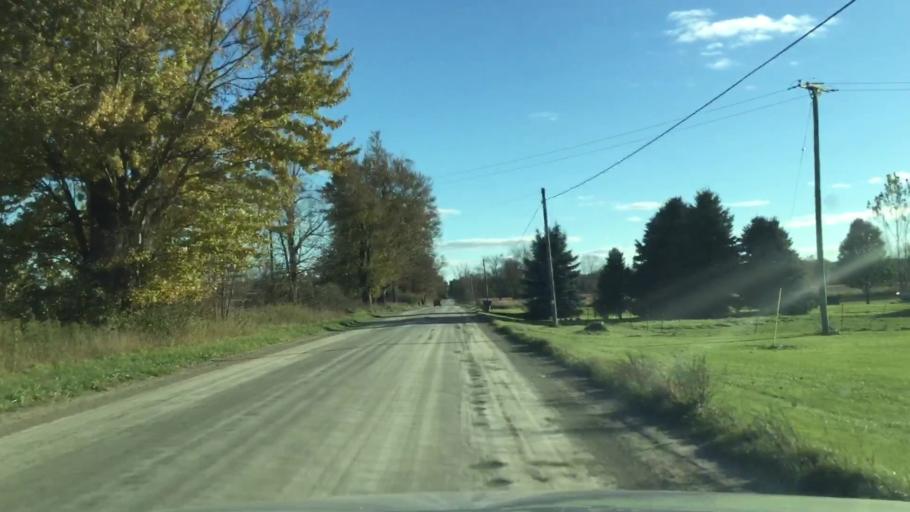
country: US
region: Michigan
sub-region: Lapeer County
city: Lapeer
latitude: 43.0647
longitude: -83.2269
